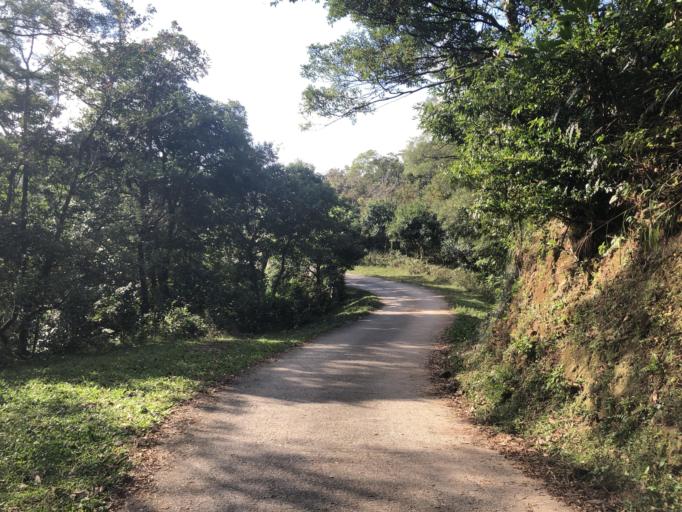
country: HK
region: Tsuen Wan
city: Tsuen Wan
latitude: 22.3994
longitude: 114.0921
